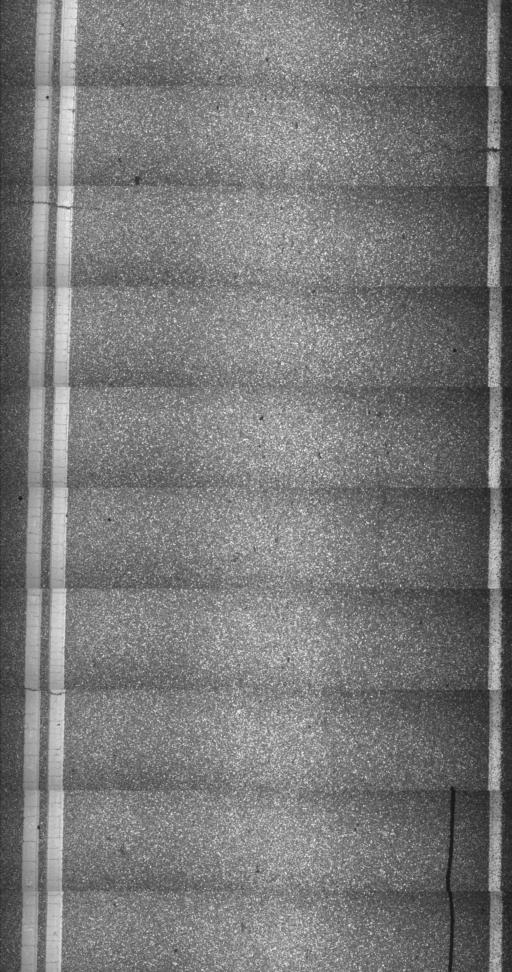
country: US
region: Vermont
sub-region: Windsor County
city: Wilder
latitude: 43.6862
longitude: -72.3211
